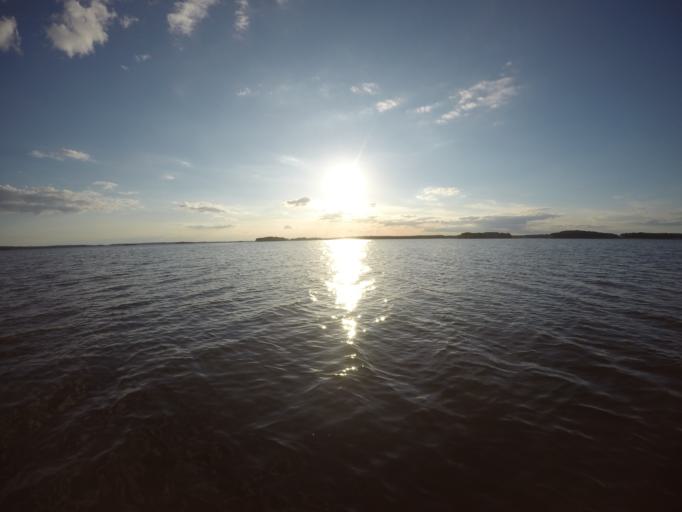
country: SE
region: Soedermanland
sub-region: Eskilstuna Kommun
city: Kvicksund
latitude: 59.4537
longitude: 16.2282
